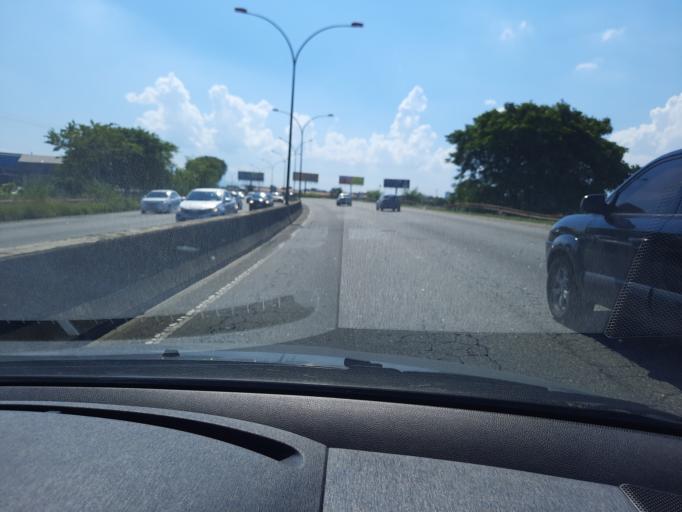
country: BR
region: Rio de Janeiro
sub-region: Duque De Caxias
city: Duque de Caxias
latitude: -22.8085
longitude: -43.2759
